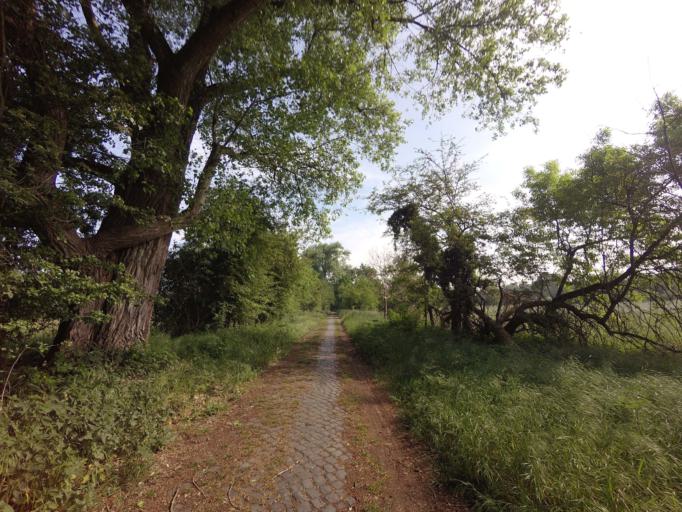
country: DE
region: Lower Saxony
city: Braunschweig
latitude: 52.3149
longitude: 10.5247
